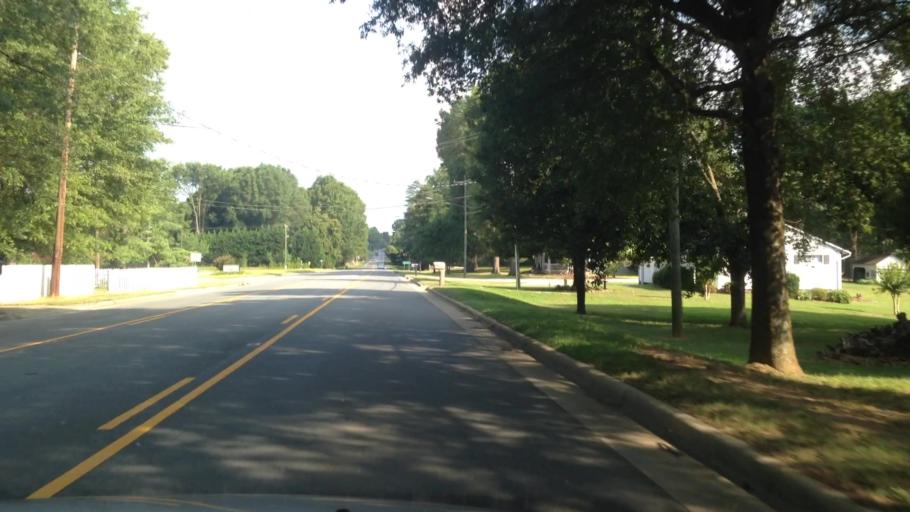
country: US
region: North Carolina
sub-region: Forsyth County
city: Kernersville
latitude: 36.1368
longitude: -80.1205
